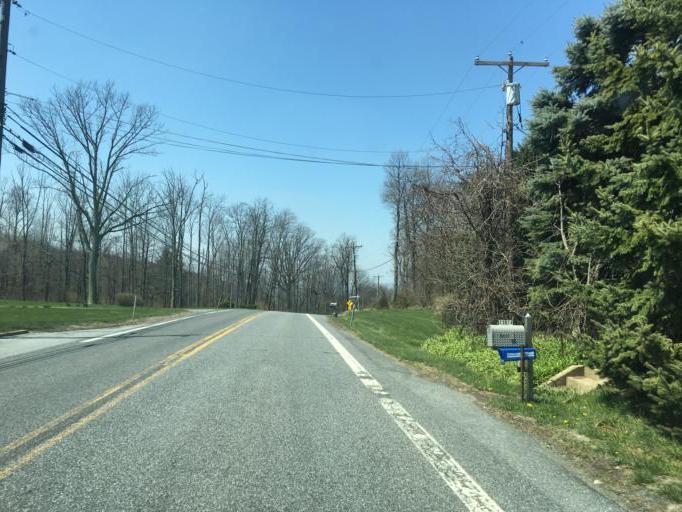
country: US
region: Maryland
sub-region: Washington County
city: Smithsburg
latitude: 39.6370
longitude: -77.5437
